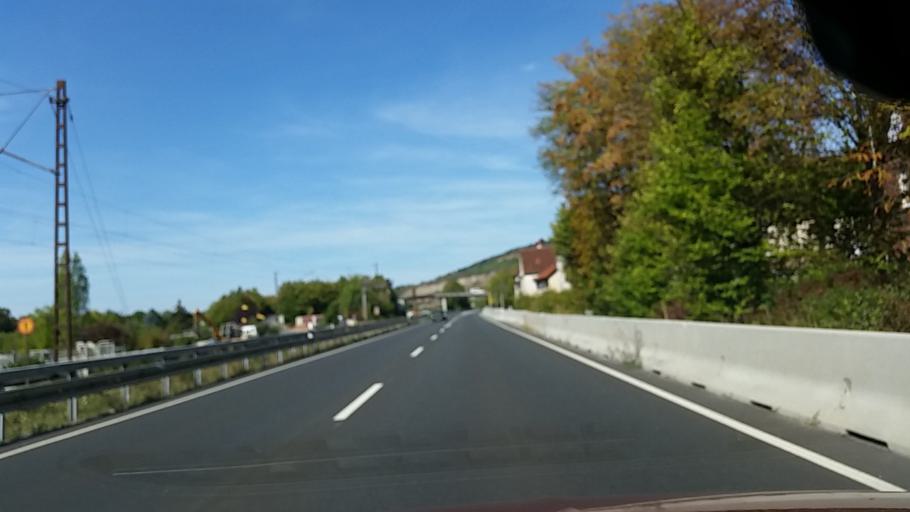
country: DE
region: Bavaria
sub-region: Regierungsbezirk Unterfranken
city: Thungersheim
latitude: 49.8791
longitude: 9.8401
